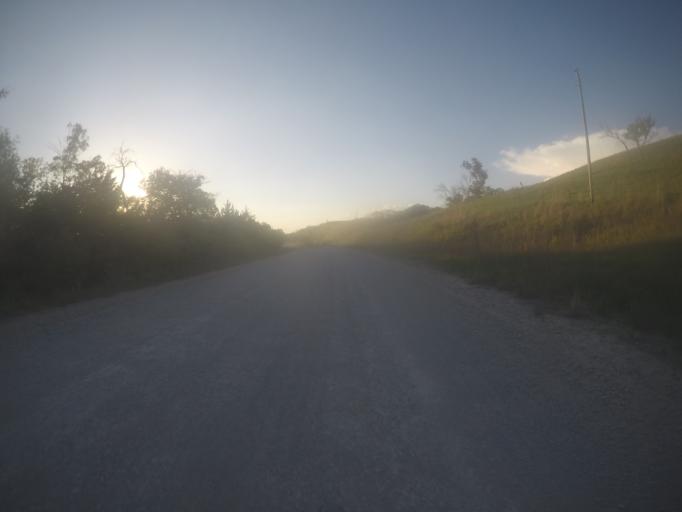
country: US
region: Kansas
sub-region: Riley County
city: Manhattan
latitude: 39.2392
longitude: -96.5584
